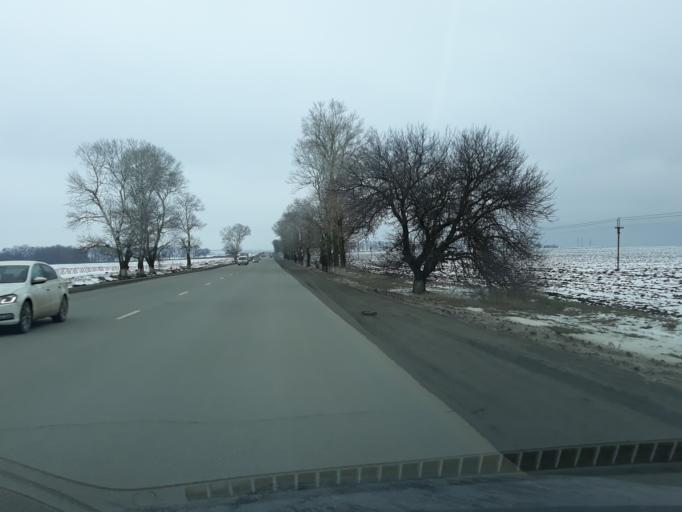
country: RU
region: Rostov
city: Sinyavskoye
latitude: 47.3021
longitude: 39.1762
